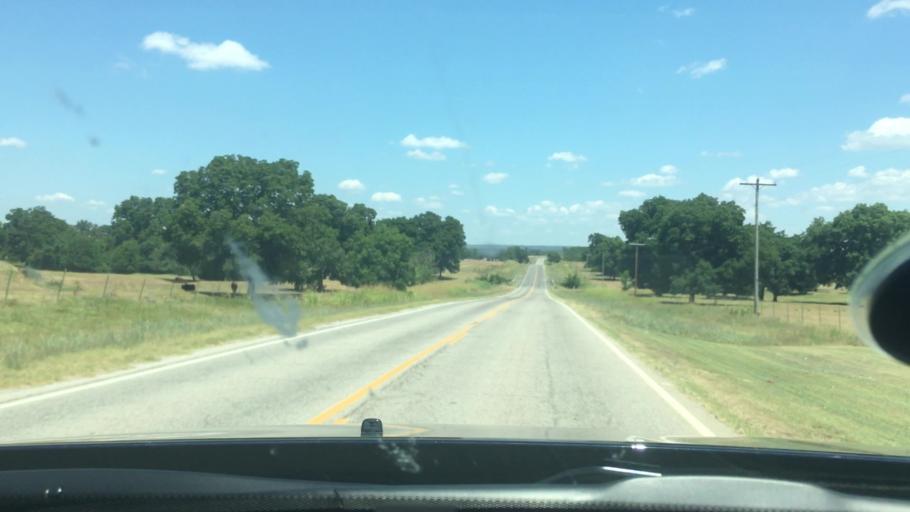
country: US
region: Oklahoma
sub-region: Carter County
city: Dickson
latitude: 34.2092
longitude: -96.9771
